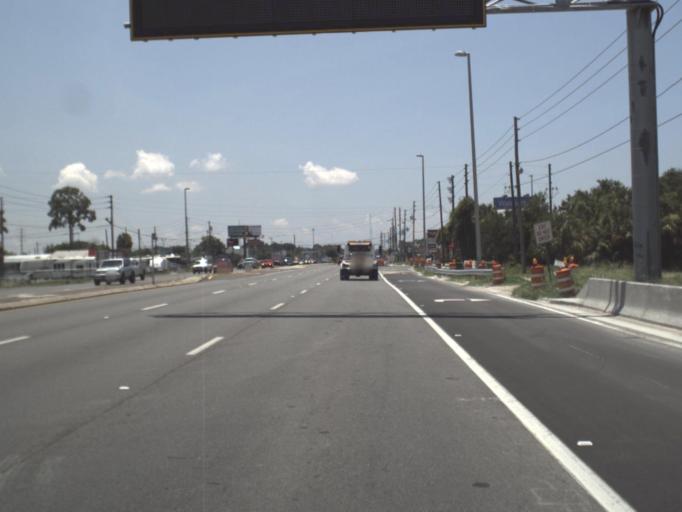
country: US
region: Florida
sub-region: Pasco County
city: Port Richey
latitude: 28.2849
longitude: -82.7147
